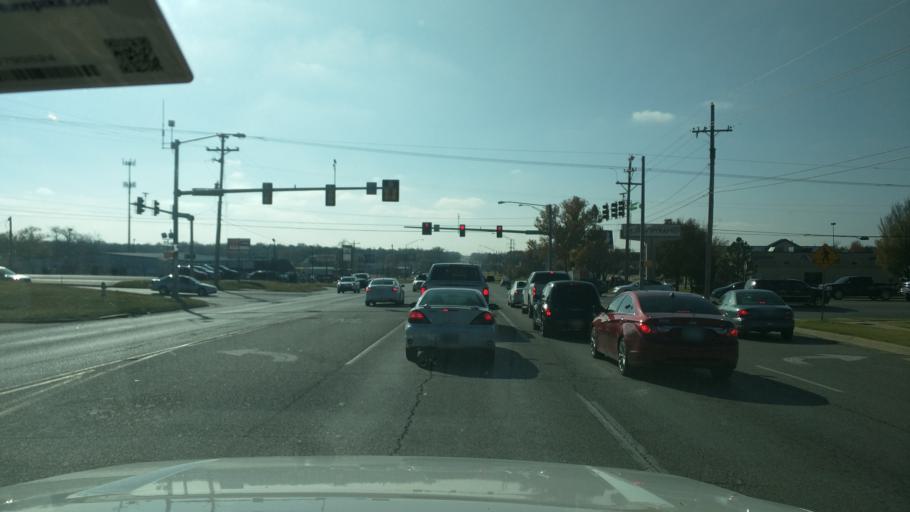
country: US
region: Oklahoma
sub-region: Washington County
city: Bartlesville
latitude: 36.7140
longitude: -95.9352
